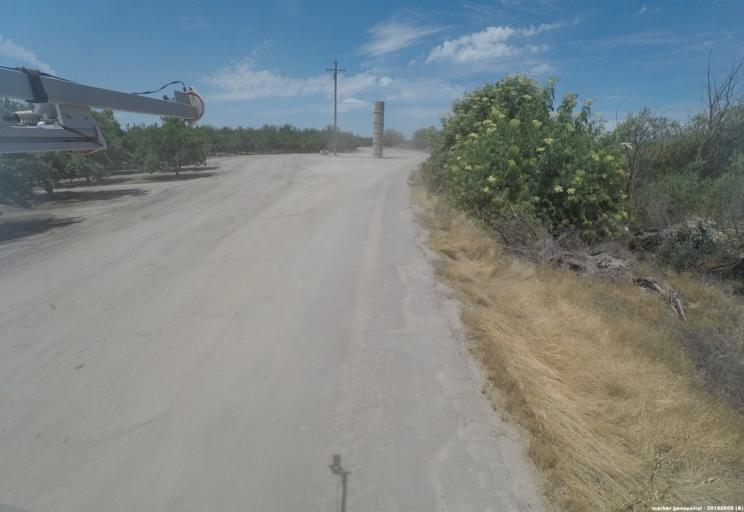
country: US
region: California
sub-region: Fresno County
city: Mendota
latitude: 36.7927
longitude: -120.3225
